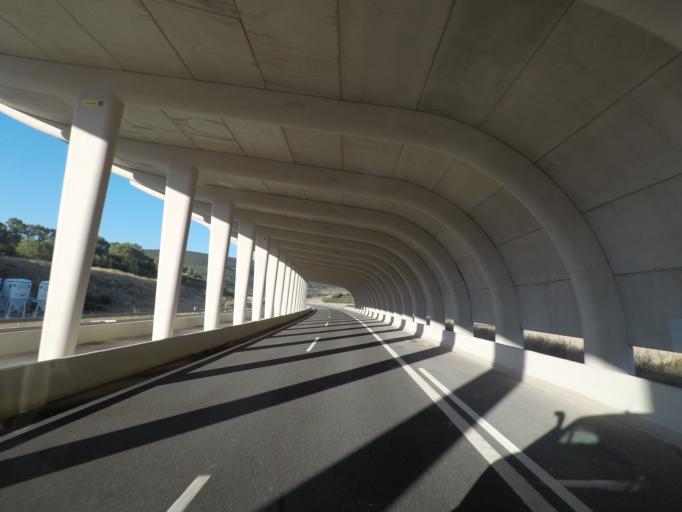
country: ES
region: Navarre
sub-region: Provincia de Navarra
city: Liedena
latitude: 42.6222
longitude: -1.2796
